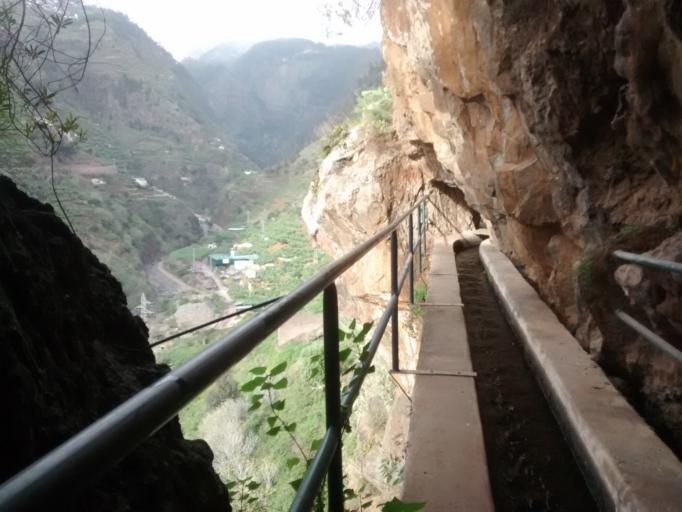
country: PT
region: Madeira
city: Camara de Lobos
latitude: 32.6589
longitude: -16.9606
